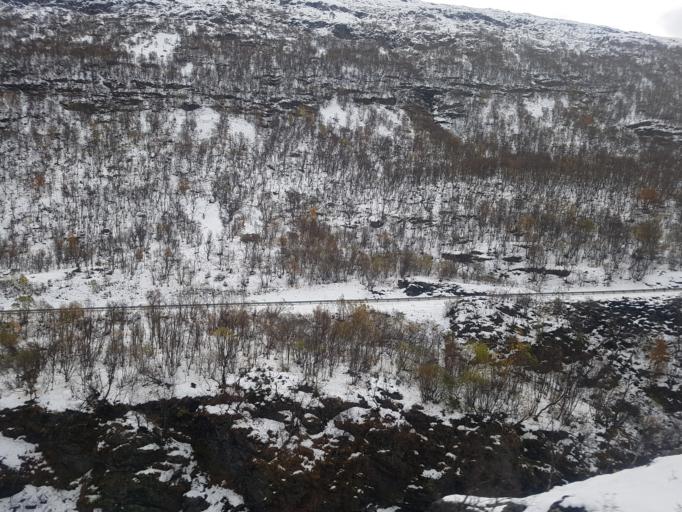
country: NO
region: Sor-Trondelag
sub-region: Oppdal
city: Oppdal
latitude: 62.3387
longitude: 9.6226
